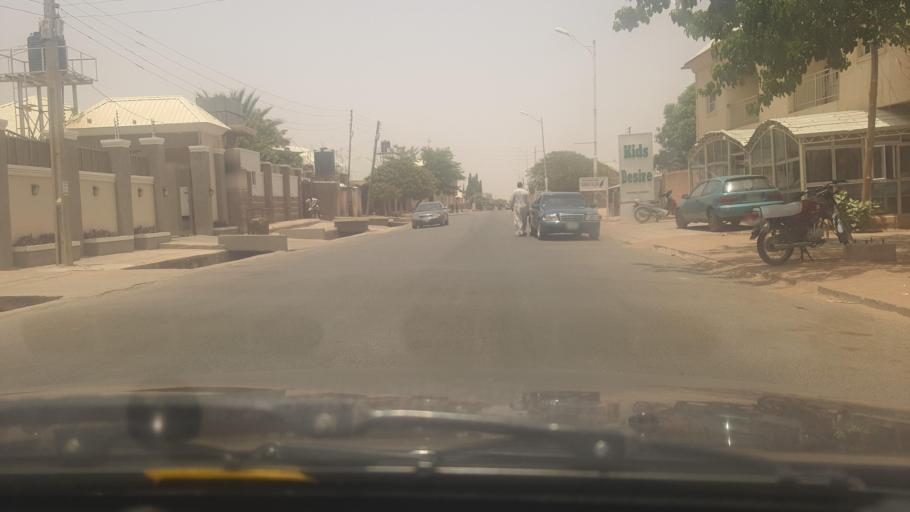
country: NG
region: Gombe
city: Gombe
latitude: 10.3041
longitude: 11.1477
